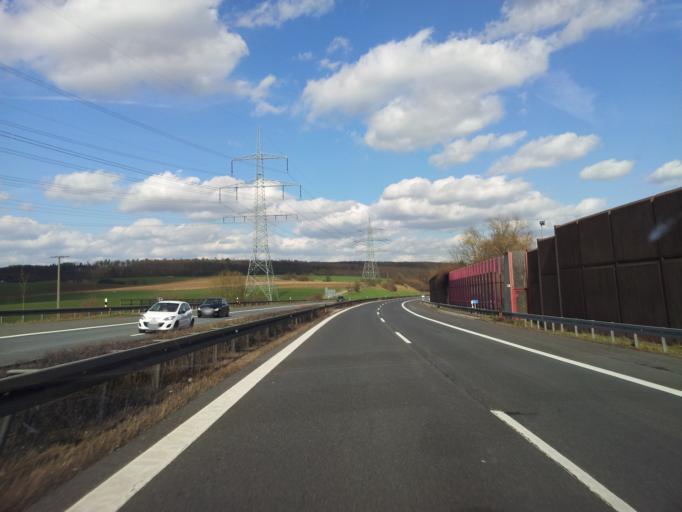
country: DE
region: Bavaria
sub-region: Upper Franconia
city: Memmelsdorf
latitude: 49.9635
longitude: 10.9892
